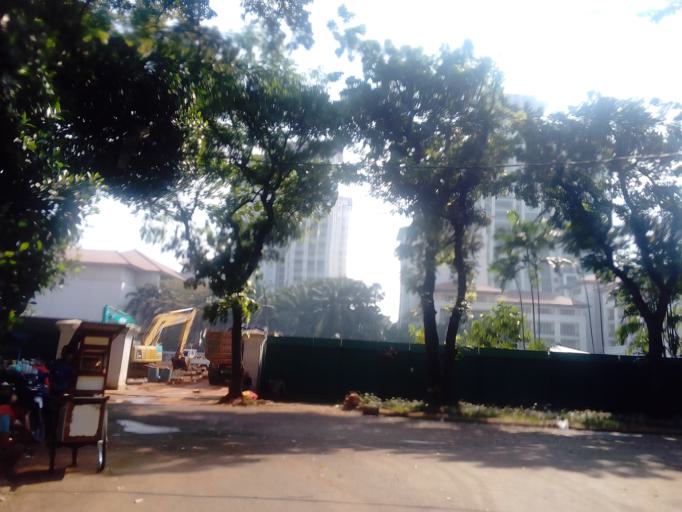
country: ID
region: Jakarta Raya
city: Jakarta
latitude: -6.2542
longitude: 106.8040
